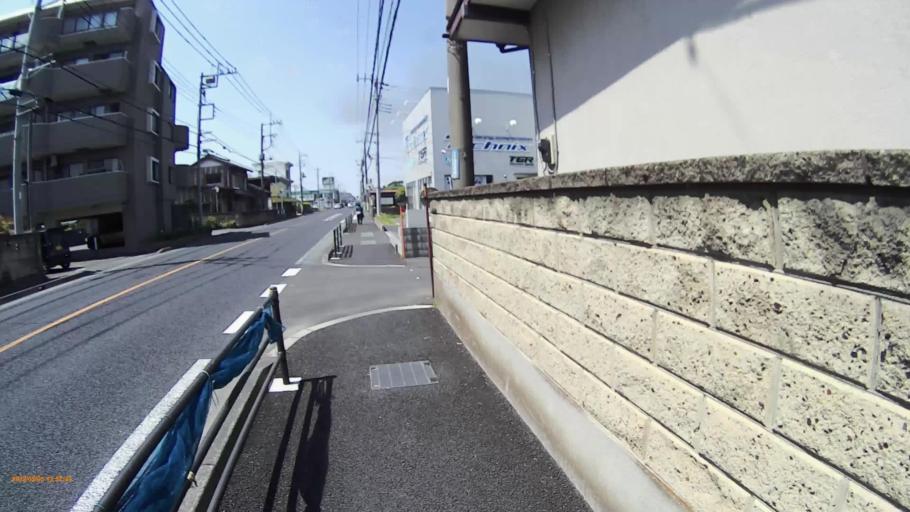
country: JP
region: Saitama
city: Kasukabe
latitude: 35.9585
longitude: 139.7748
